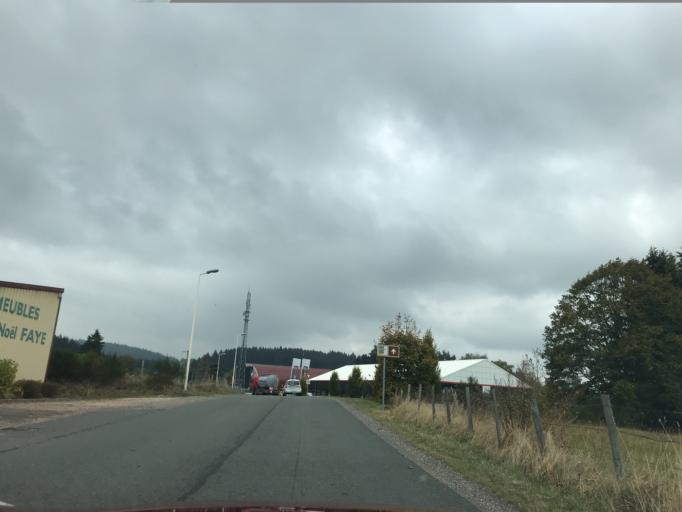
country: FR
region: Rhone-Alpes
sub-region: Departement de la Loire
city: Noiretable
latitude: 45.8191
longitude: 3.7590
